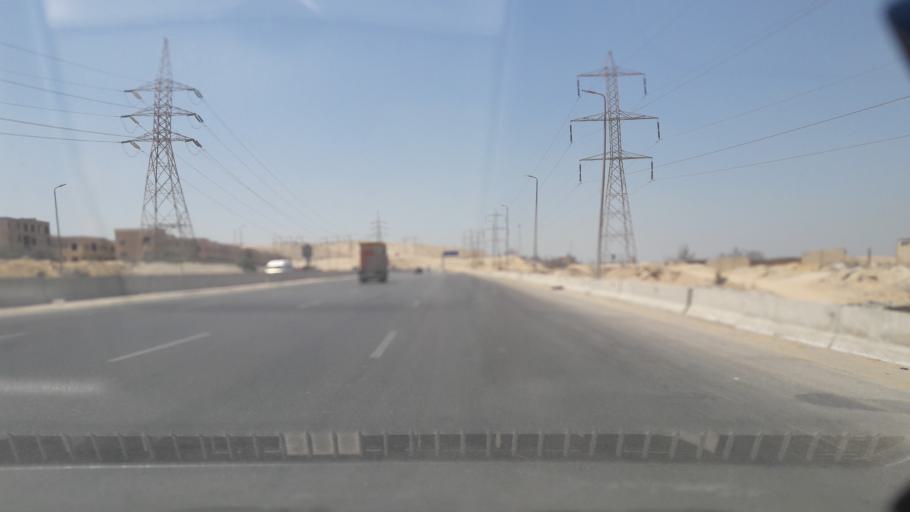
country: EG
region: Al Jizah
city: Awsim
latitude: 30.0201
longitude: 31.0821
